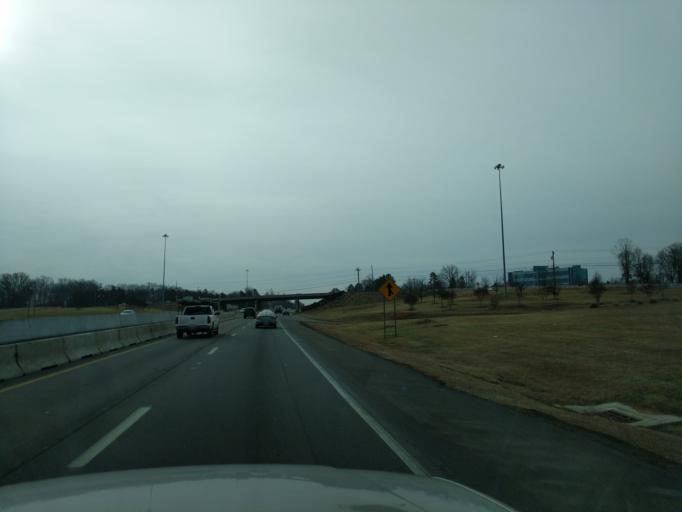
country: US
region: North Carolina
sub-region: Iredell County
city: Mooresville
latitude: 35.5557
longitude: -80.8581
